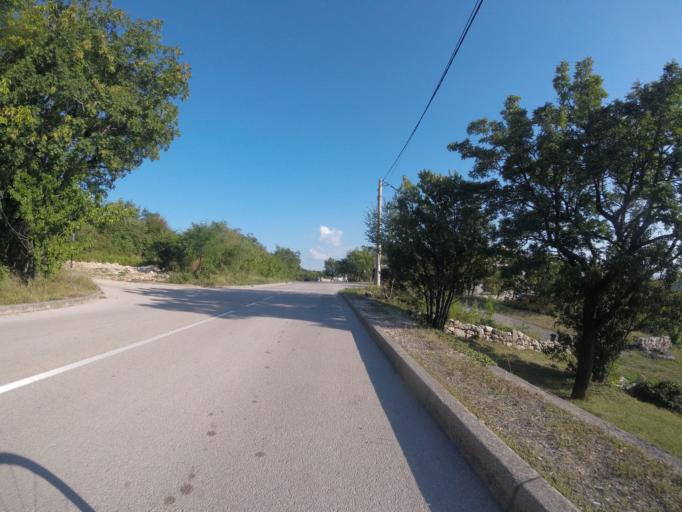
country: HR
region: Primorsko-Goranska
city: Selce
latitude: 45.1889
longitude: 14.7283
